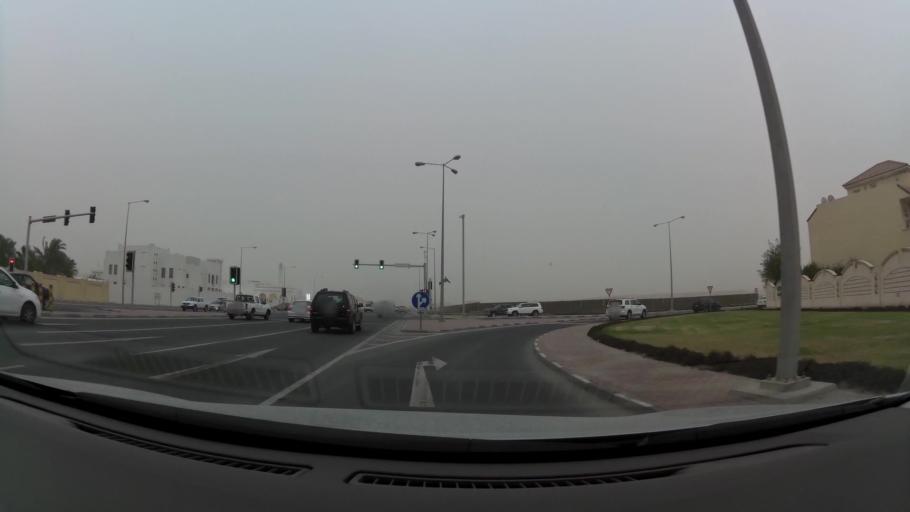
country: QA
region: Baladiyat ad Dawhah
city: Doha
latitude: 25.2451
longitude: 51.4927
